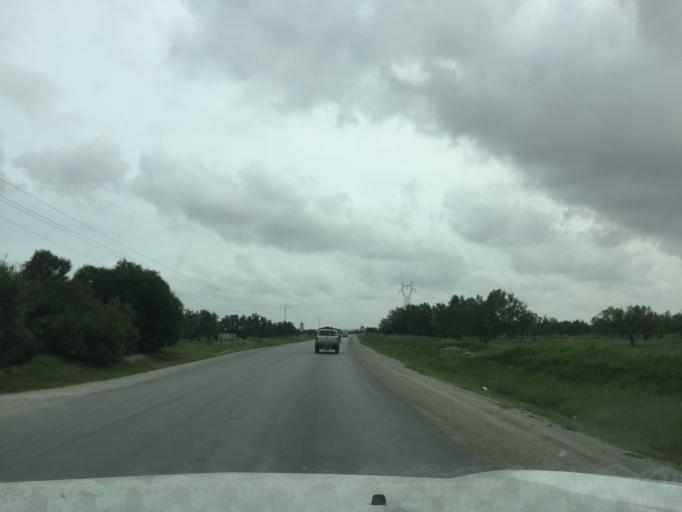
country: TN
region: Al Munastir
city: Manzil Kamil
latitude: 35.6261
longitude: 10.6980
